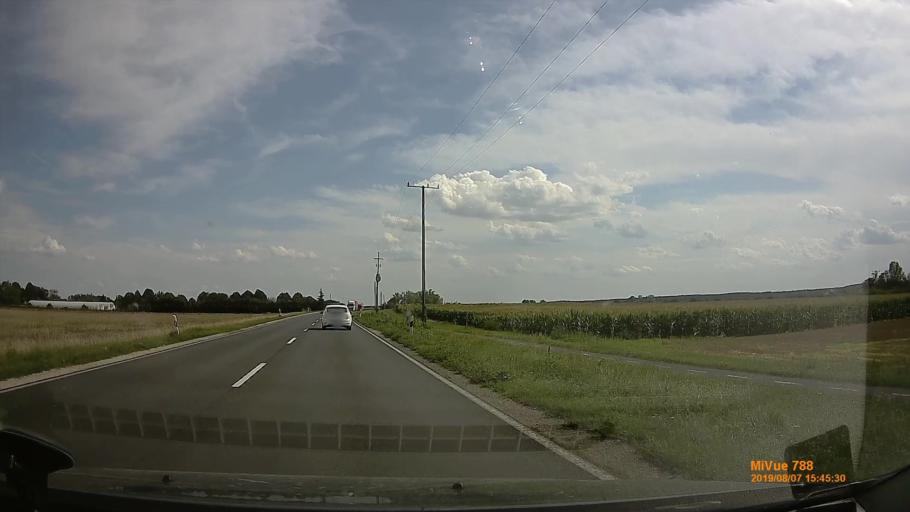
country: HU
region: Vas
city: Szombathely
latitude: 47.1967
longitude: 16.6194
